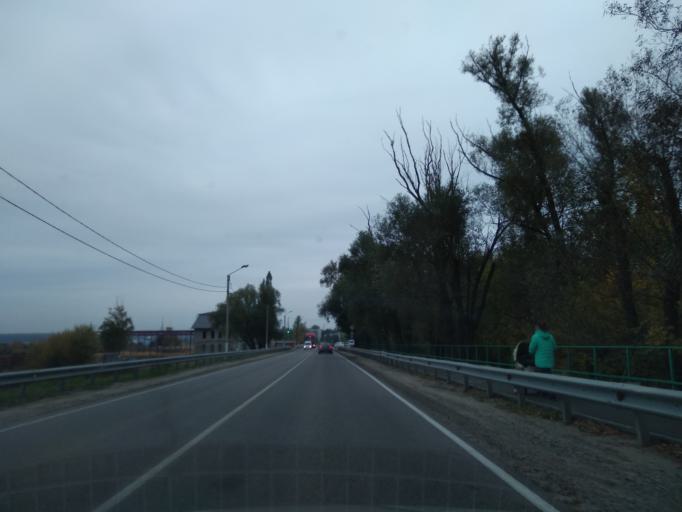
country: RU
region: Lipetsk
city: Zadonsk
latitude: 52.3873
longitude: 38.9360
